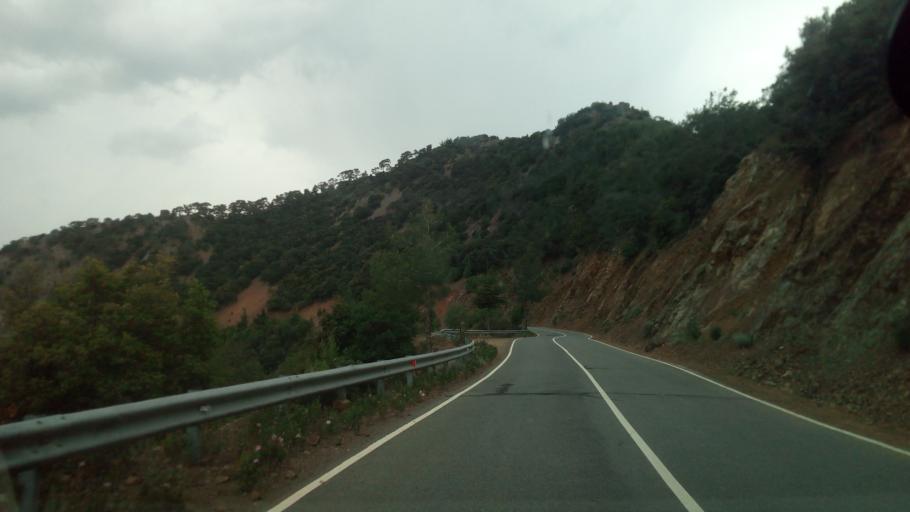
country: CY
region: Lefkosia
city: Kato Pyrgos
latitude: 35.0056
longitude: 32.7060
